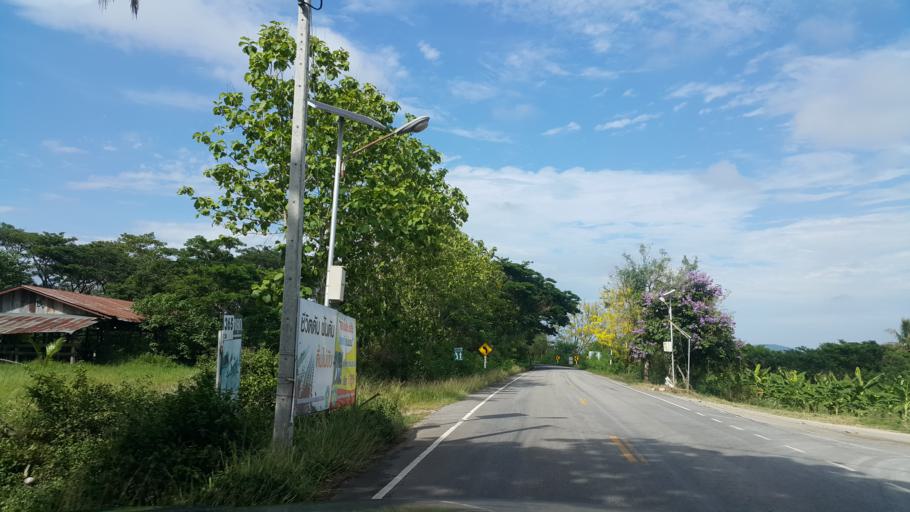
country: TH
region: Chiang Rai
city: Wiang Chai
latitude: 19.9395
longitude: 99.9181
